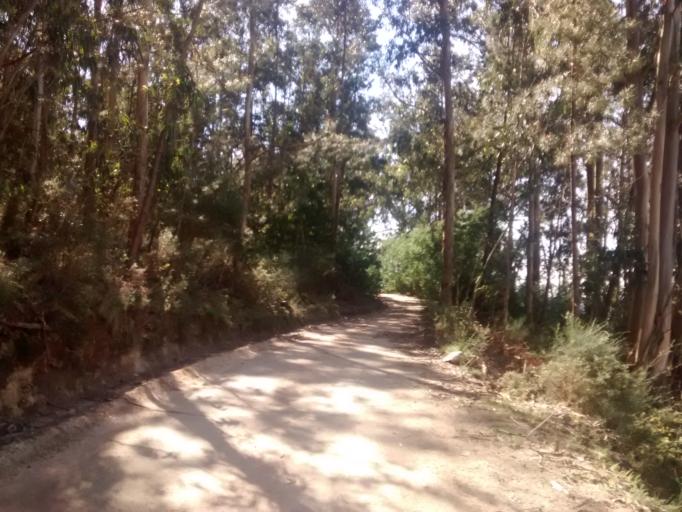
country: ES
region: Galicia
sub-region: Provincia de Pontevedra
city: O Grove
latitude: 42.4876
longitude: -8.8829
